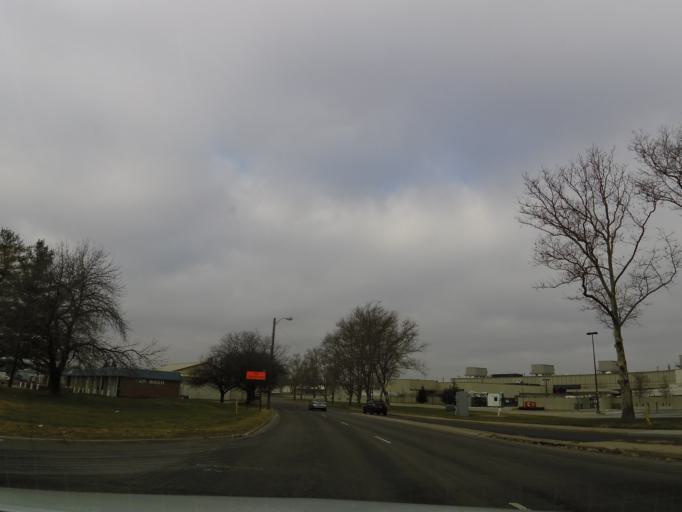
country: US
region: Indiana
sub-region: Bartholomew County
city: Columbus
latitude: 39.2008
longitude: -85.9104
